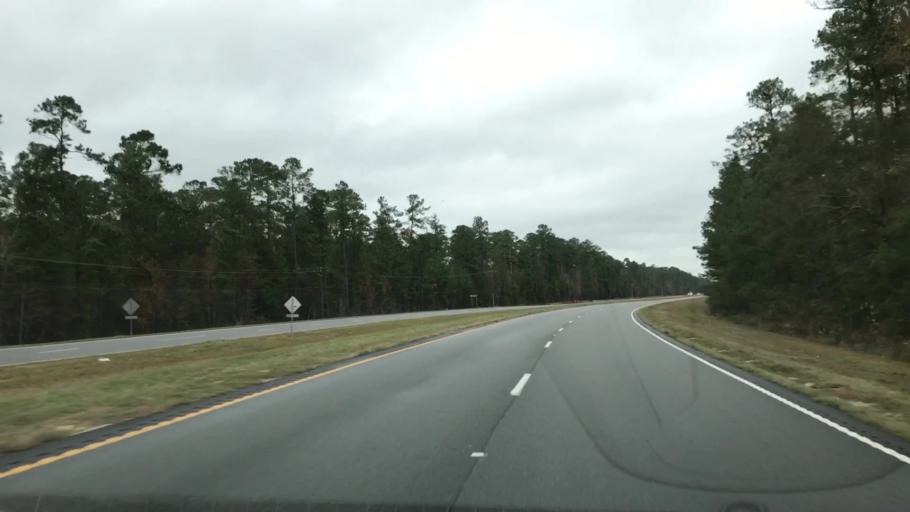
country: US
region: South Carolina
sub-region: Georgetown County
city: Georgetown
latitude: 33.2523
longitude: -79.3740
